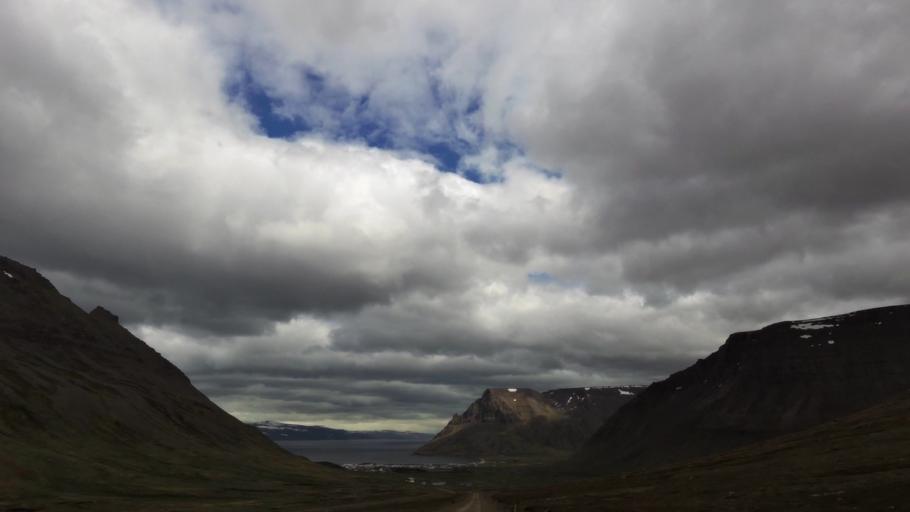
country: IS
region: Westfjords
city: Isafjoerdur
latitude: 66.1631
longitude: -23.3183
